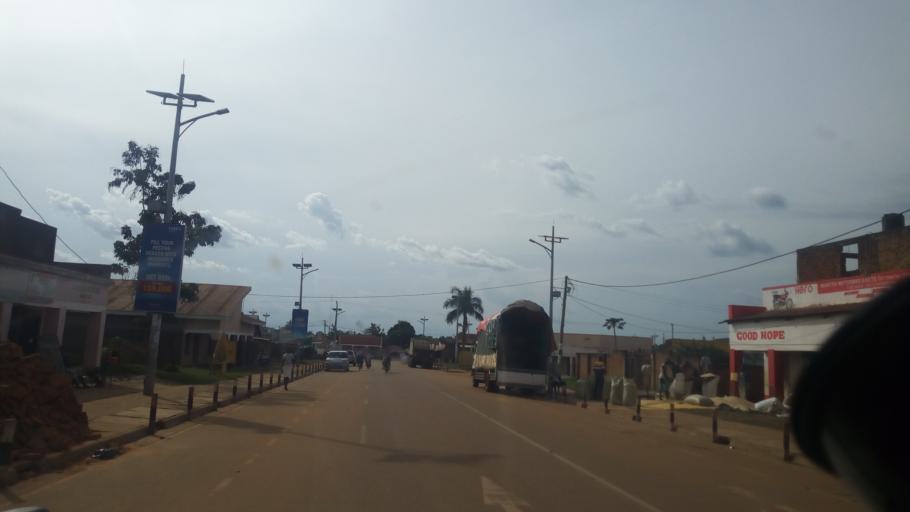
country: UG
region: Northern Region
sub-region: Lira District
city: Lira
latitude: 2.2384
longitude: 32.8911
